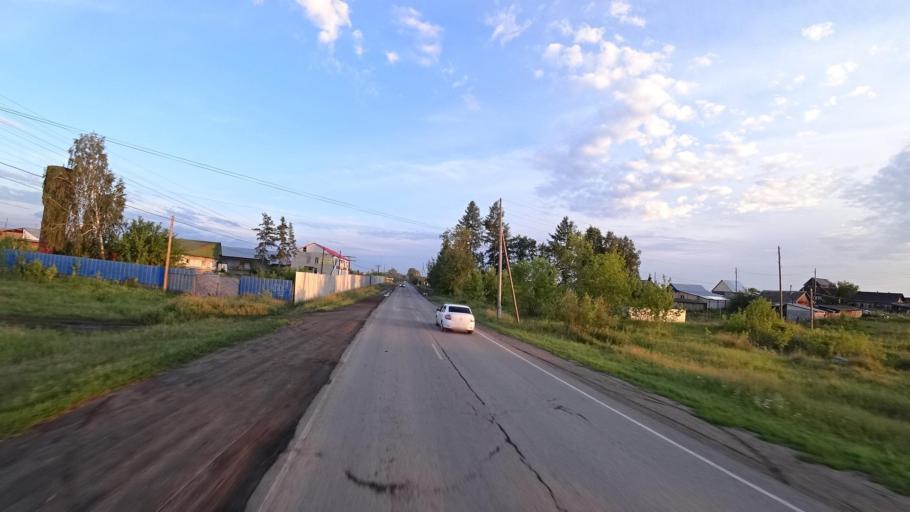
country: RU
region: Sverdlovsk
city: Kamyshlov
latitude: 56.8655
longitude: 62.7104
